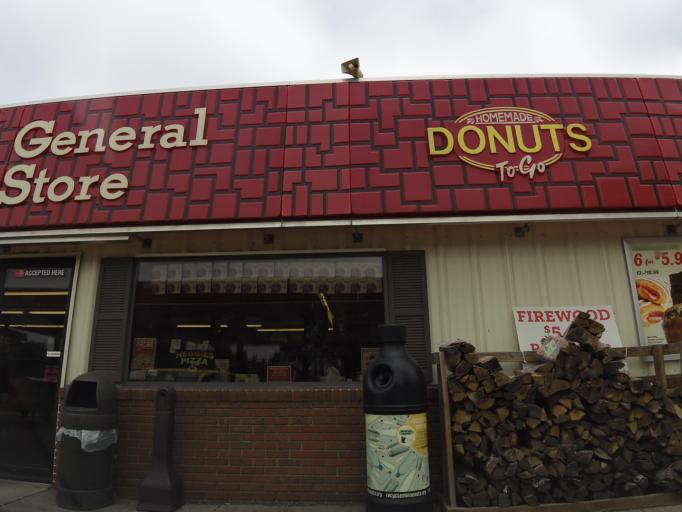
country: US
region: Minnesota
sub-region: Renville County
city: Olivia
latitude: 44.7769
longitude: -94.9860
